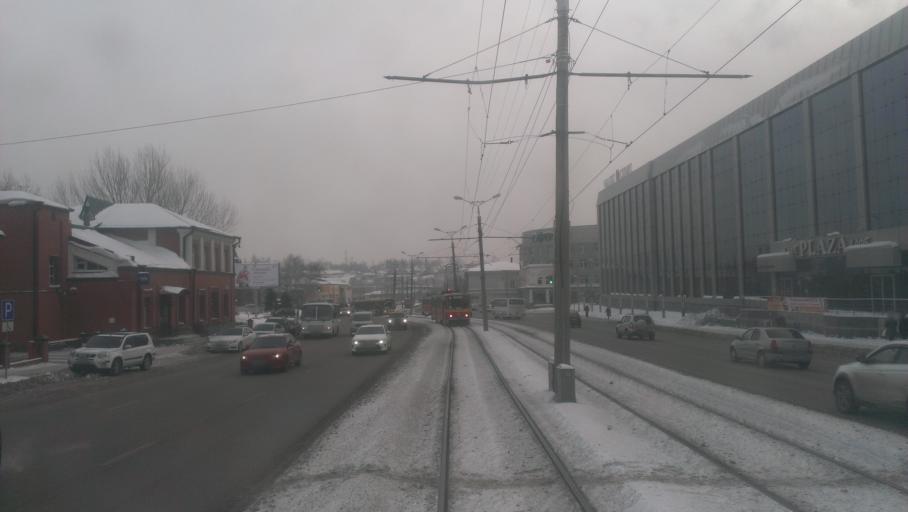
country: RU
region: Altai Krai
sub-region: Gorod Barnaulskiy
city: Barnaul
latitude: 53.3313
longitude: 83.7818
